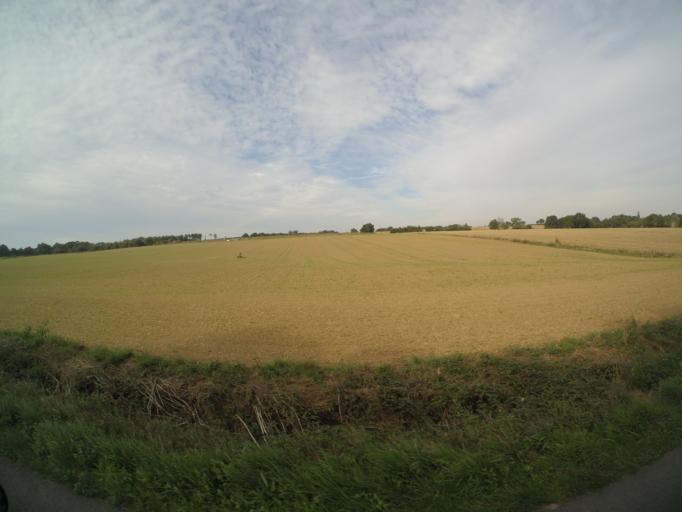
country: FR
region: Pays de la Loire
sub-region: Departement de Maine-et-Loire
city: La Chapelle-du-Genet
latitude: 47.1761
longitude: -1.0444
